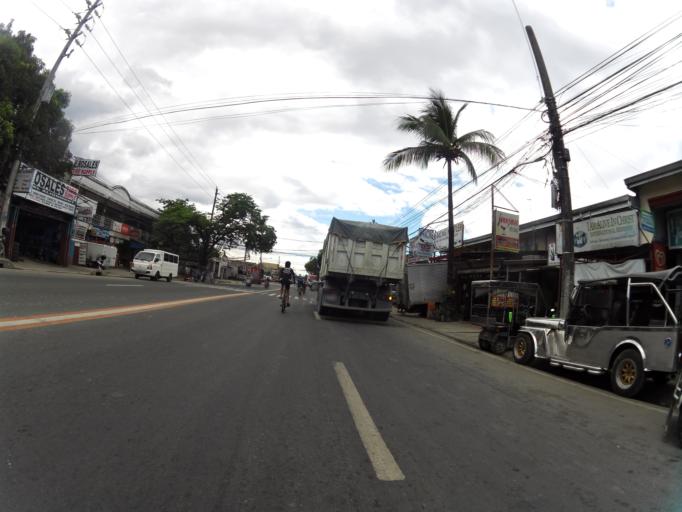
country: PH
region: Calabarzon
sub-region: Province of Rizal
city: Antipolo
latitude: 14.6325
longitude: 121.1142
